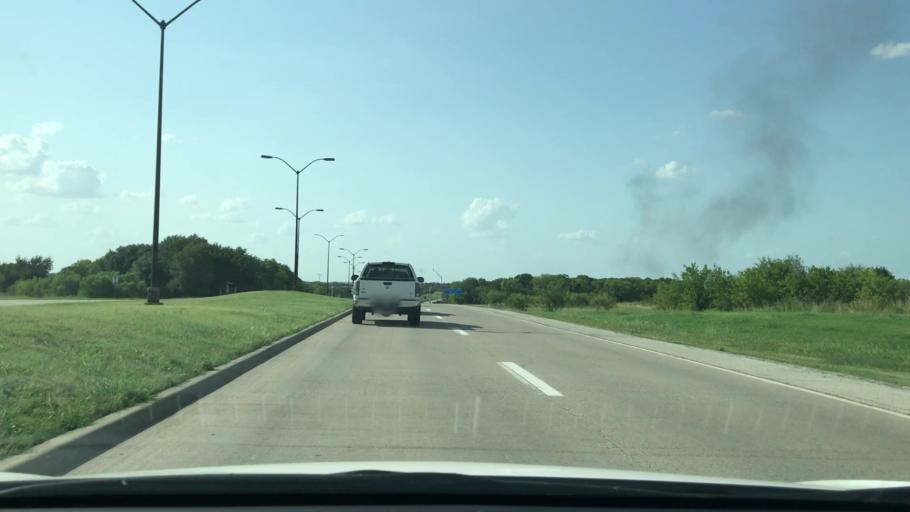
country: US
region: Texas
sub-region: Tarrant County
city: Euless
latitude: 32.8660
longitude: -97.0530
